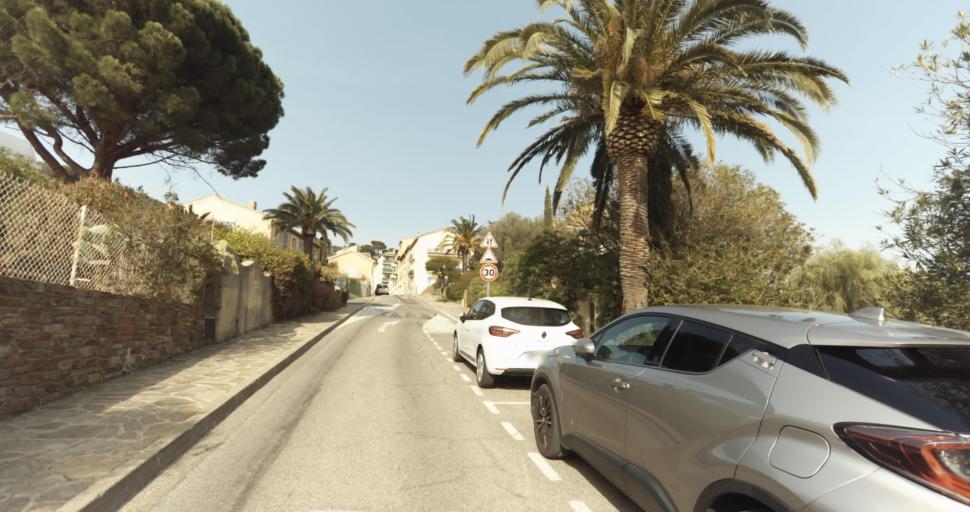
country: FR
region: Provence-Alpes-Cote d'Azur
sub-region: Departement du Var
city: Bormes-les-Mimosas
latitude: 43.1487
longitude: 6.3413
